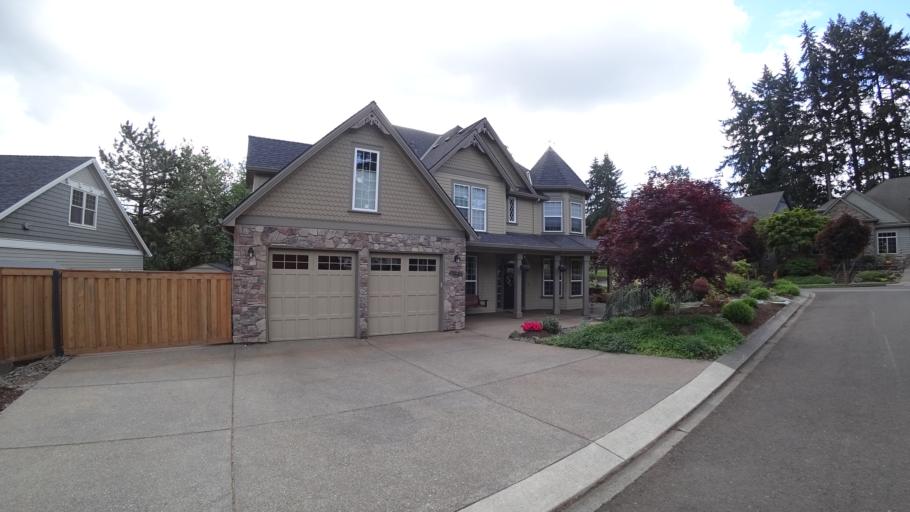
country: US
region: Oregon
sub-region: Washington County
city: Beaverton
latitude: 45.4699
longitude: -122.8346
